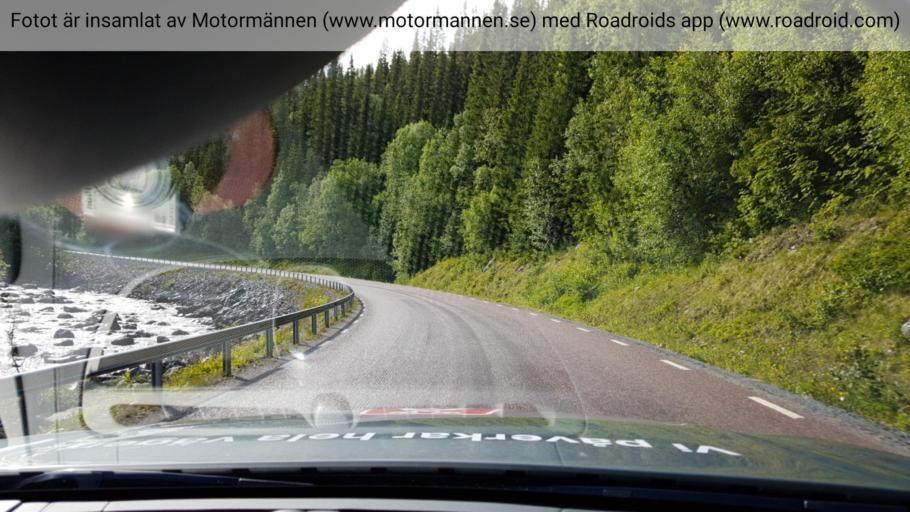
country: SE
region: Jaemtland
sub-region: Are Kommun
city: Jarpen
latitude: 63.1045
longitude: 13.8401
